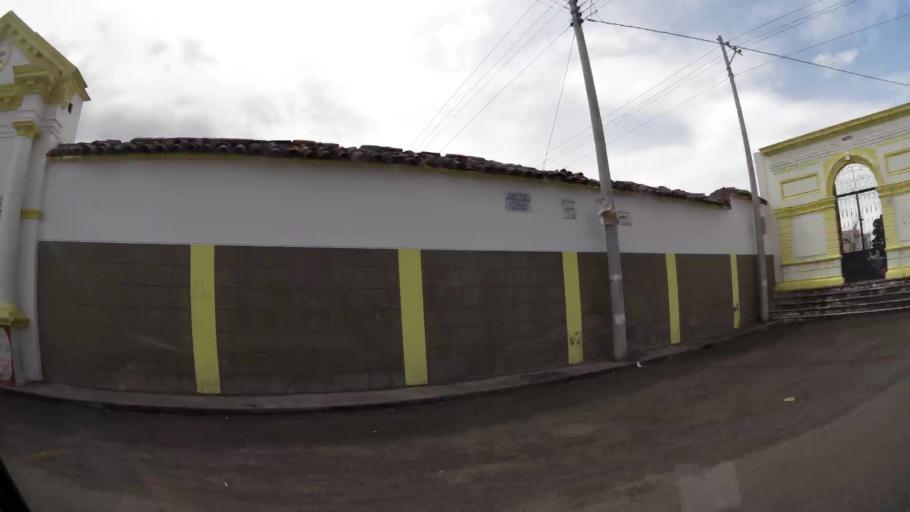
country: EC
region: Cotopaxi
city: Latacunga
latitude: -0.9281
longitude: -78.6170
